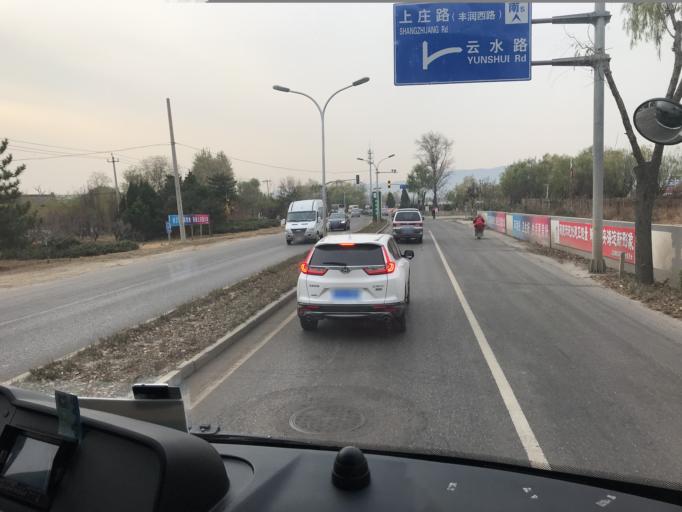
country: CN
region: Beijing
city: Wenquan
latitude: 40.0799
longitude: 116.2105
